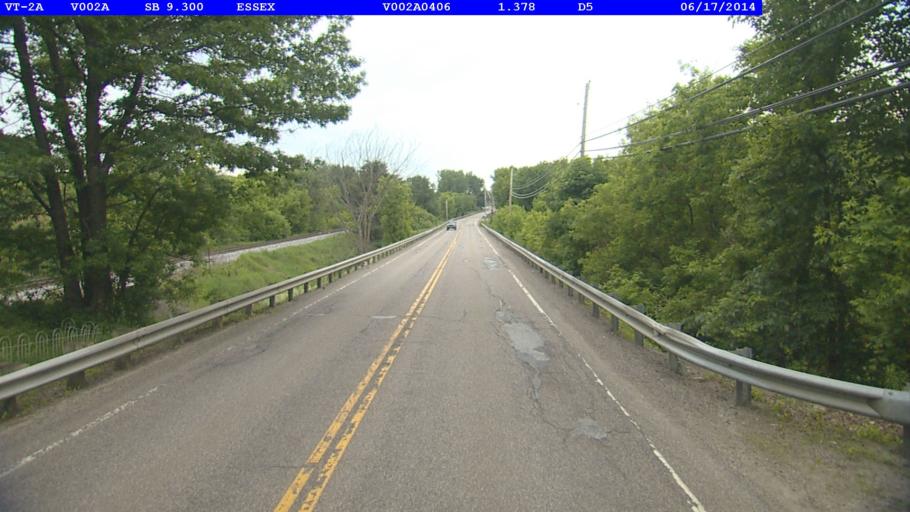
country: US
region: Vermont
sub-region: Chittenden County
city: Essex Junction
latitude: 44.5005
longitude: -73.1140
